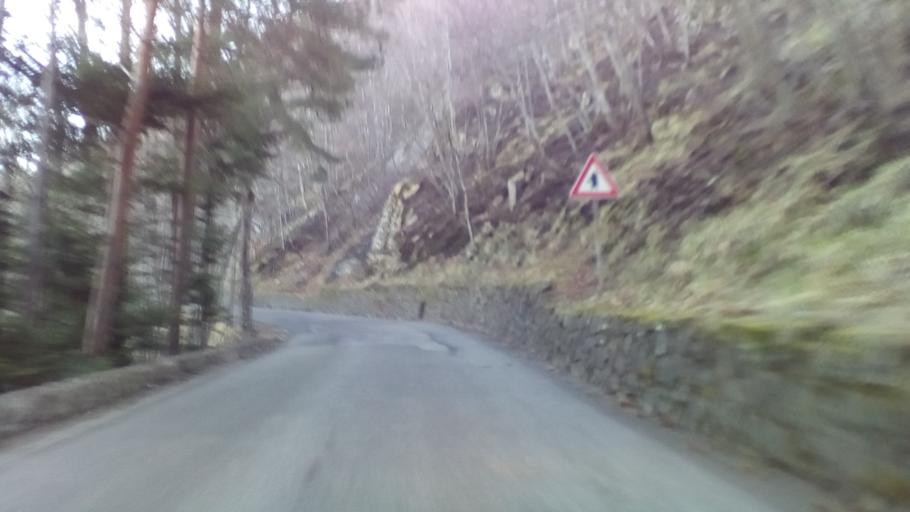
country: IT
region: Tuscany
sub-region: Provincia di Lucca
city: Castiglione di Garfagnana
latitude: 44.1657
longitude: 10.4429
